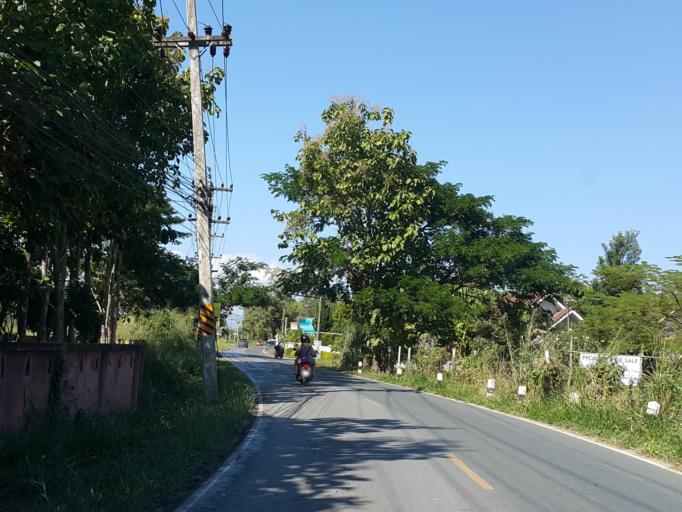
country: TH
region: Chiang Mai
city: San Sai
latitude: 18.9424
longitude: 98.9293
